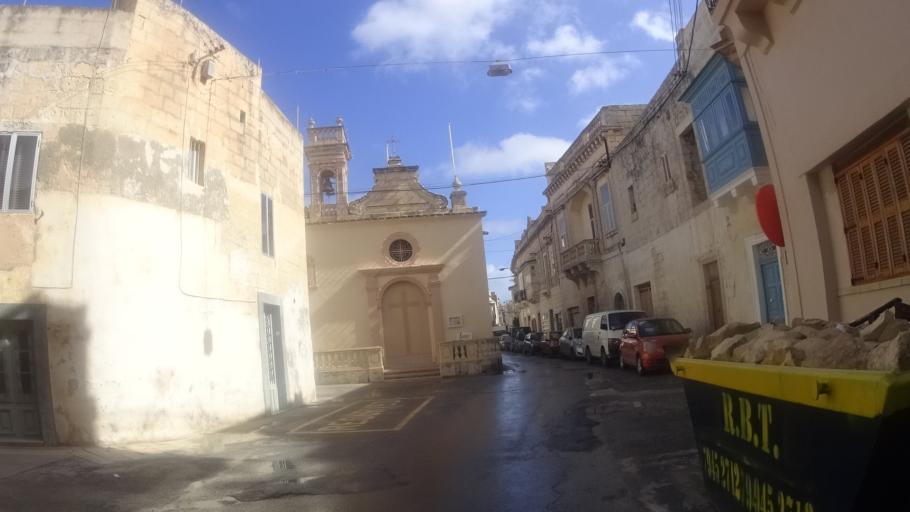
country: MT
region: In-Naxxar
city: Naxxar
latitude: 35.9148
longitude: 14.4415
